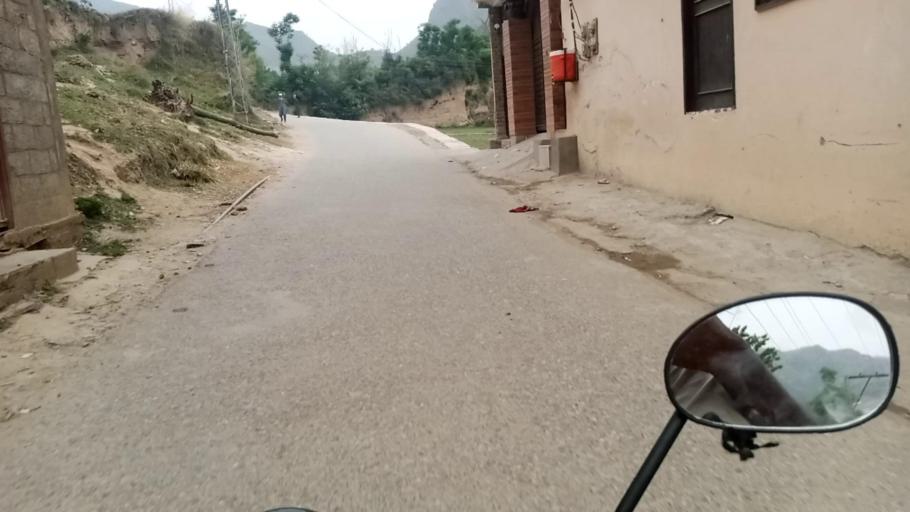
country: PK
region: Khyber Pakhtunkhwa
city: Saidu Sharif
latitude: 34.7567
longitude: 72.3787
